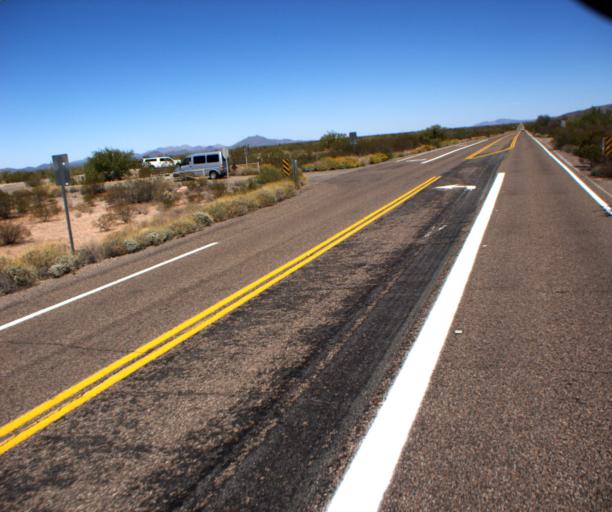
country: US
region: Arizona
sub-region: Pima County
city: Ajo
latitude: 32.1295
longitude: -112.7677
